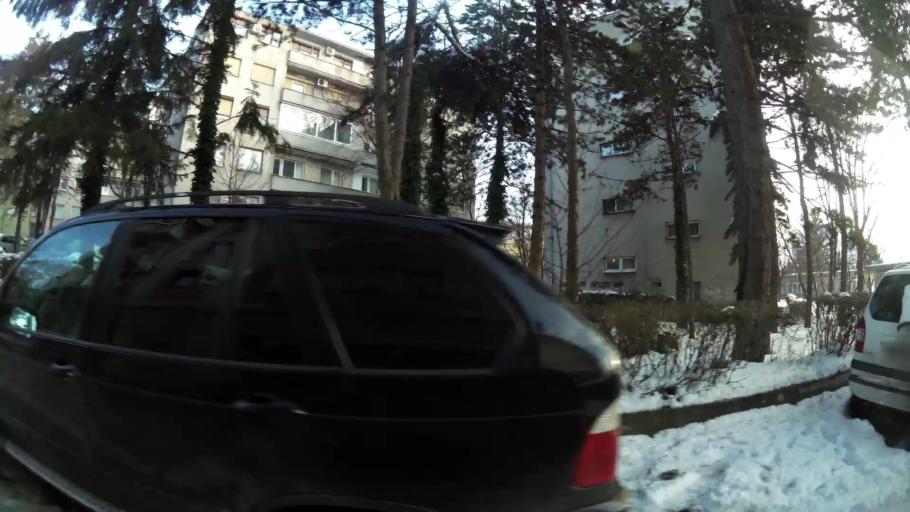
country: RS
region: Central Serbia
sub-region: Belgrade
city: Palilula
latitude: 44.8048
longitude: 20.4945
